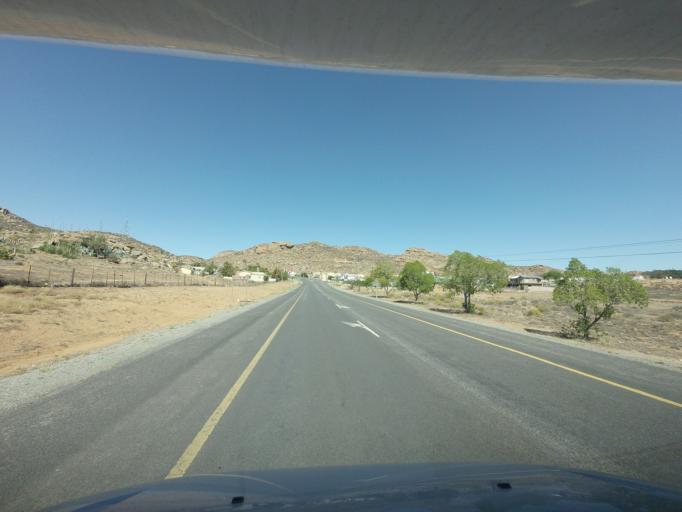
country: ZA
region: Northern Cape
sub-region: Namakwa District Municipality
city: Springbok
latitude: -29.6616
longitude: 17.8968
